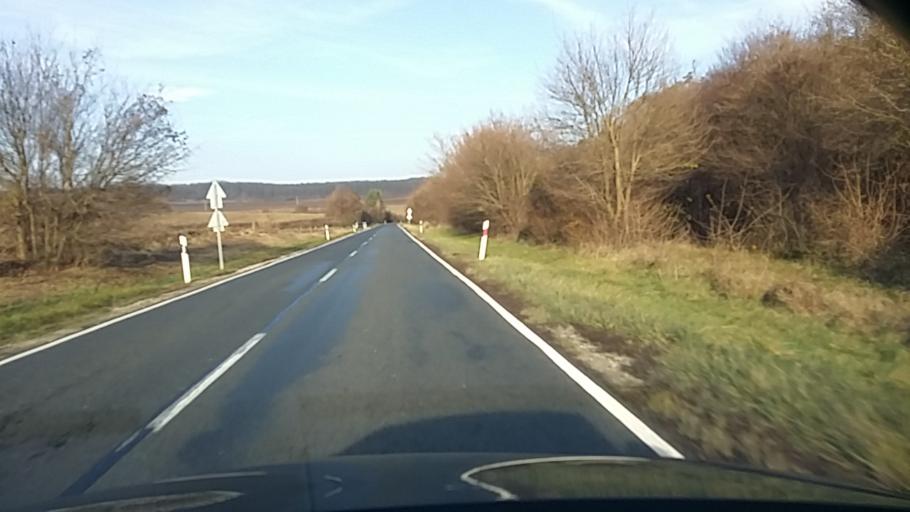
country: HU
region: Veszprem
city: Urkut
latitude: 46.9936
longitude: 17.6350
